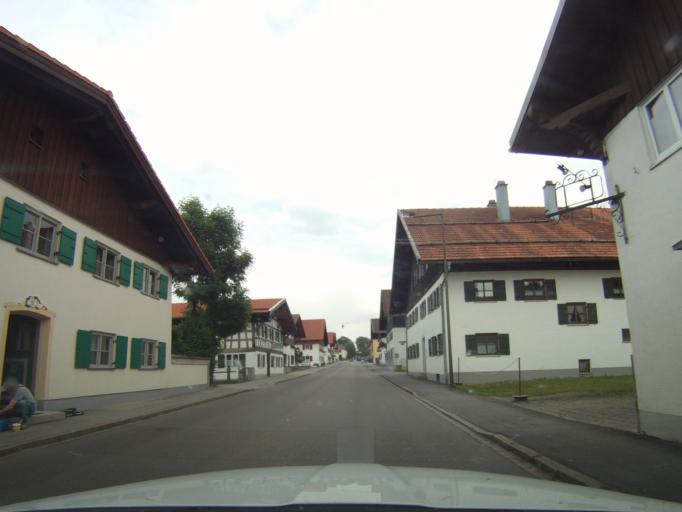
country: DE
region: Bavaria
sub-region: Swabia
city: Nesselwang
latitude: 47.6212
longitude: 10.5023
